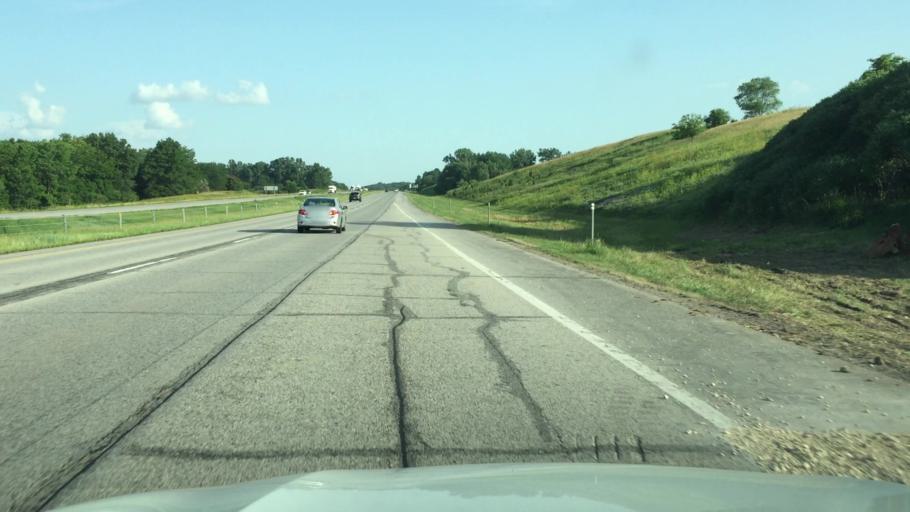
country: US
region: Iowa
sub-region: Linn County
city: Ely
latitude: 41.8427
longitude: -91.6660
